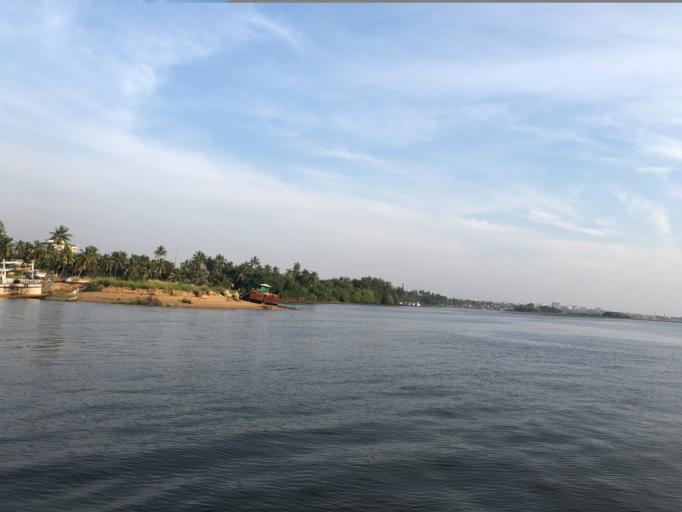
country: IN
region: Karnataka
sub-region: Dakshina Kannada
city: Mangalore
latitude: 12.8870
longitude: 74.8194
